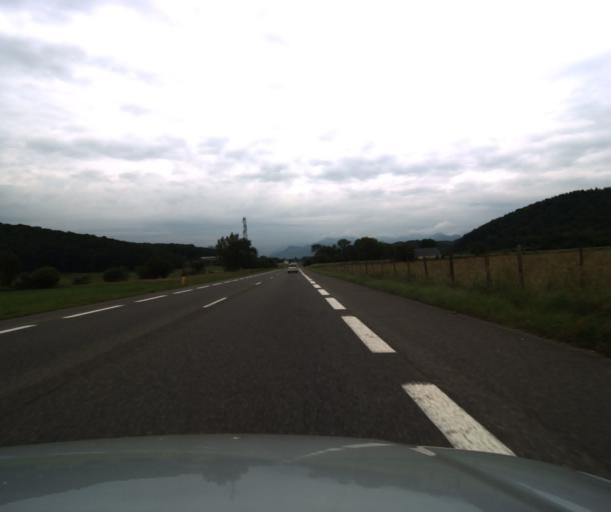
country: FR
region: Midi-Pyrenees
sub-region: Departement des Hautes-Pyrenees
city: Ossun
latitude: 43.1517
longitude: -0.0223
